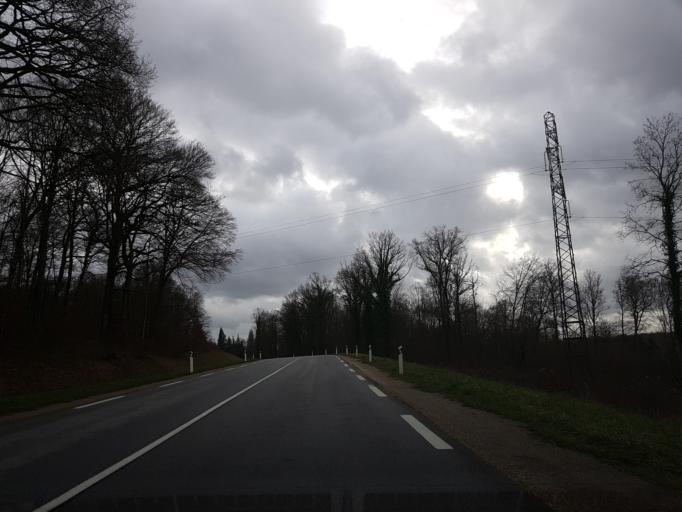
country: FR
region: Champagne-Ardenne
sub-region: Departement de la Haute-Marne
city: Fayl-Billot
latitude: 47.8037
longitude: 5.5590
